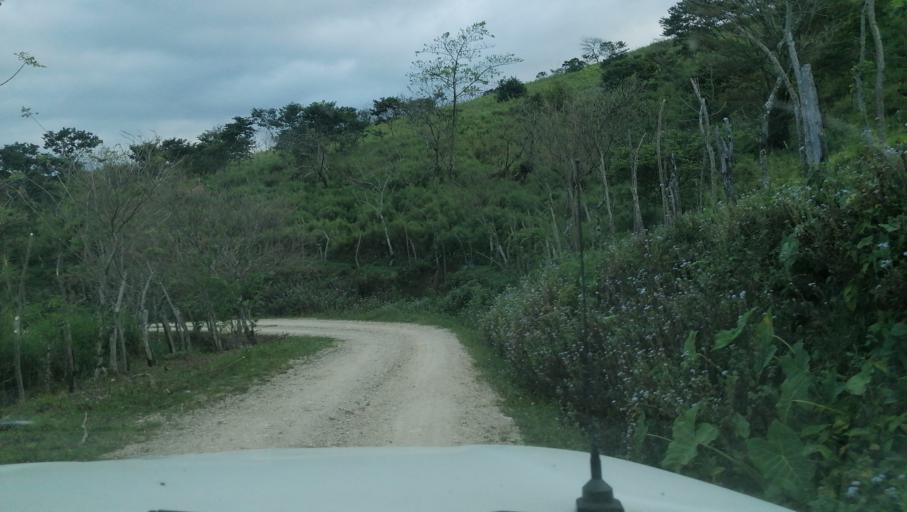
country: MX
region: Chiapas
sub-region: Francisco Leon
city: San Miguel la Sardina
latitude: 17.3026
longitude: -93.2665
